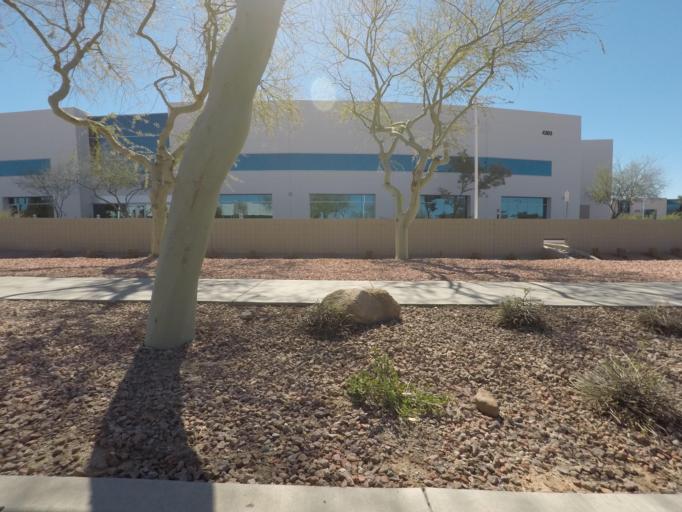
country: US
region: Arizona
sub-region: Maricopa County
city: Guadalupe
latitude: 33.4020
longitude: -111.9879
